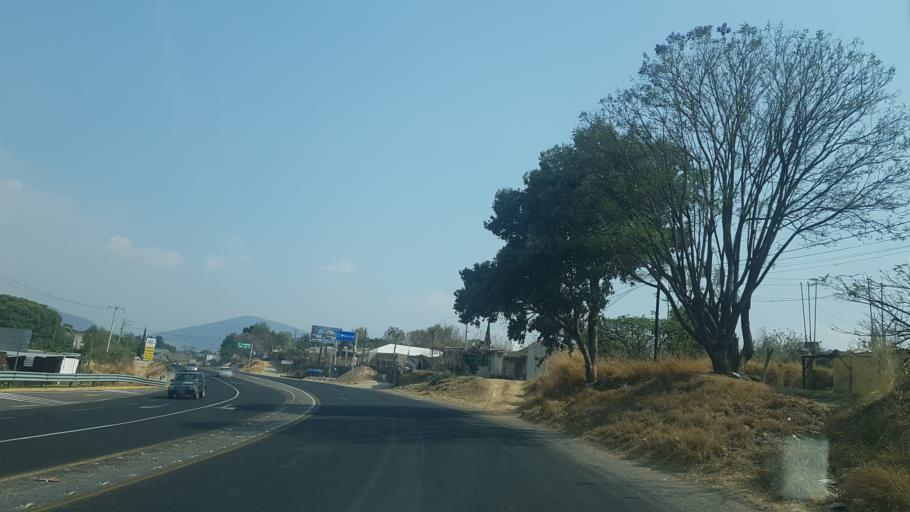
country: MX
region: Puebla
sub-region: Atlixco
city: San Agustin Huixaxtla
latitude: 18.9244
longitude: -98.4112
